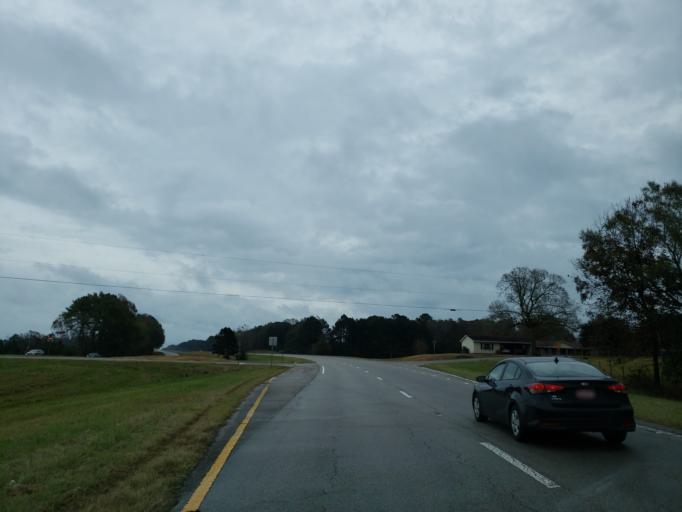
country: US
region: Mississippi
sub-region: Jones County
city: Sharon
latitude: 31.6973
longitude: -88.8942
